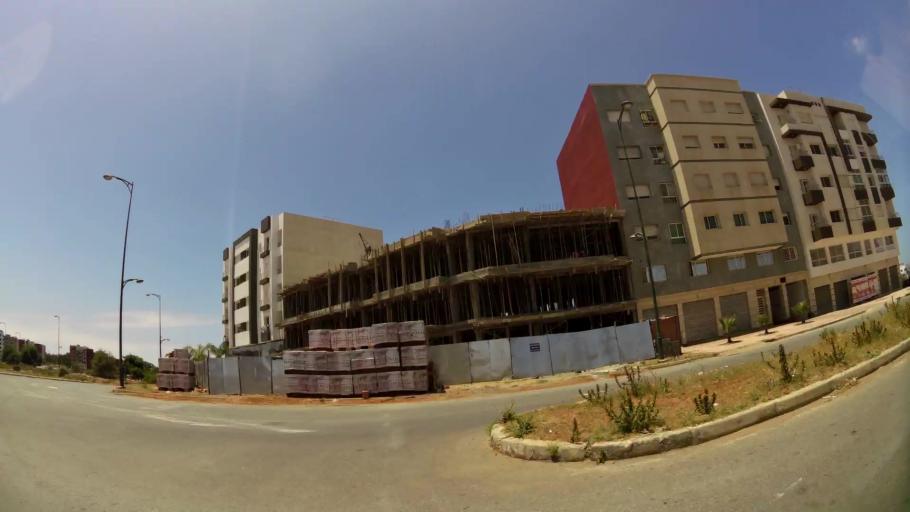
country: MA
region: Gharb-Chrarda-Beni Hssen
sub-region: Kenitra Province
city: Kenitra
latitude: 34.2652
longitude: -6.6261
